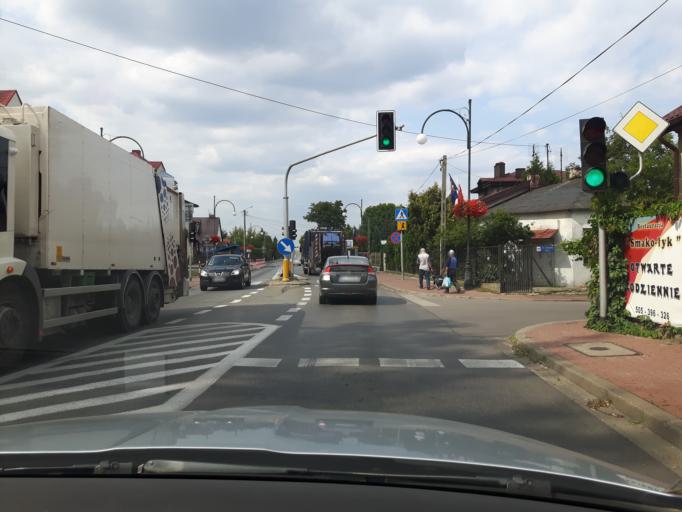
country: PL
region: Masovian Voivodeship
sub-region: Powiat legionowski
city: Nieporet
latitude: 52.4208
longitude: 21.0360
